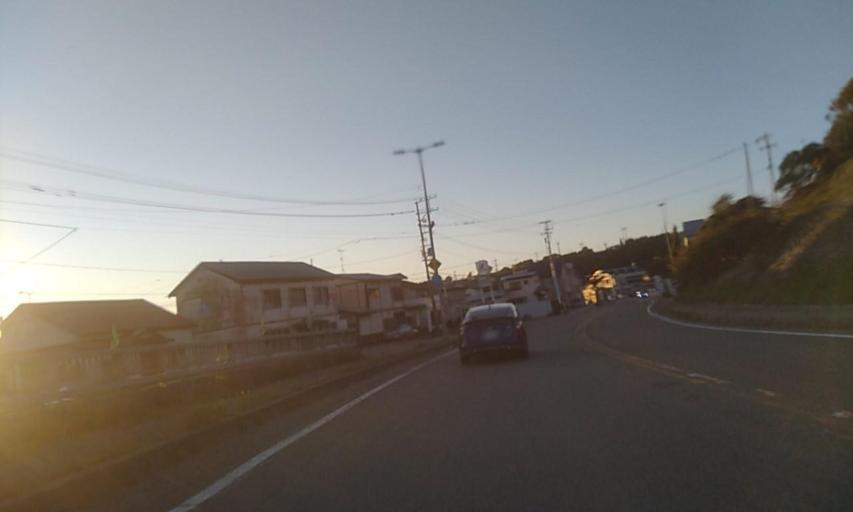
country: JP
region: Hokkaido
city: Shizunai-furukawacho
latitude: 42.1588
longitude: 142.7822
